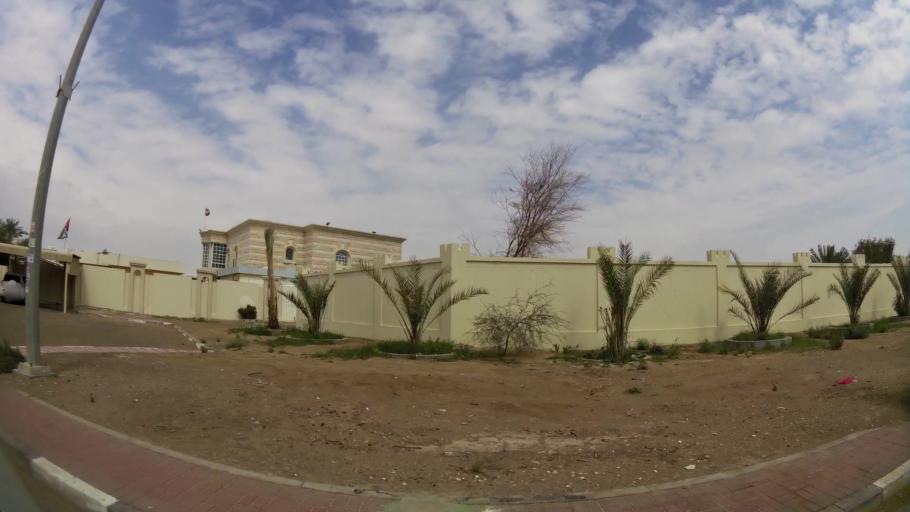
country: AE
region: Abu Dhabi
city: Al Ain
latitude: 24.1959
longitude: 55.7903
